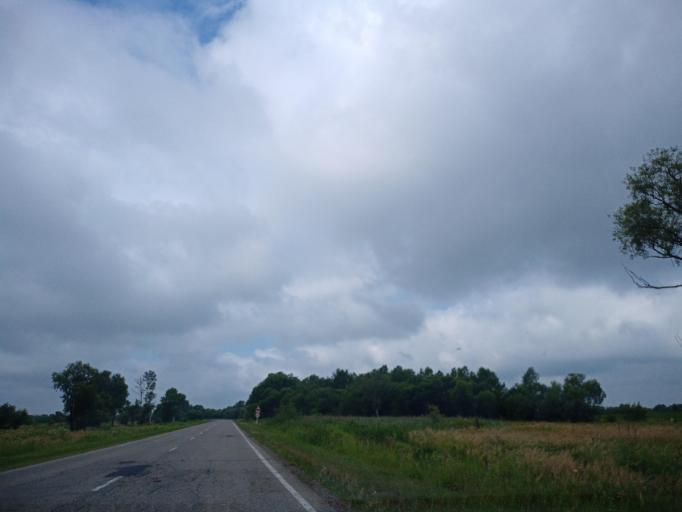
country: RU
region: Primorskiy
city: Dal'nerechensk
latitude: 45.9468
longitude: 133.8919
